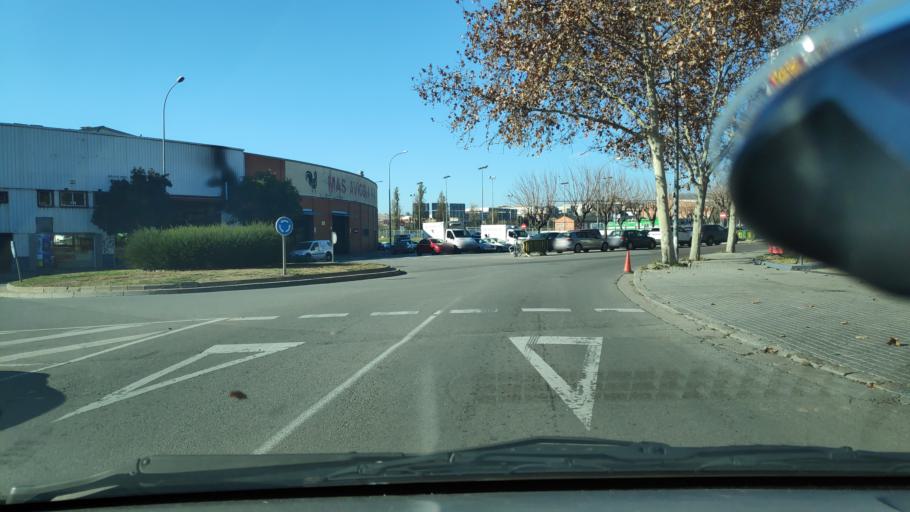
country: ES
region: Catalonia
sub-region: Provincia de Barcelona
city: Sabadell
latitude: 41.5332
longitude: 2.1002
